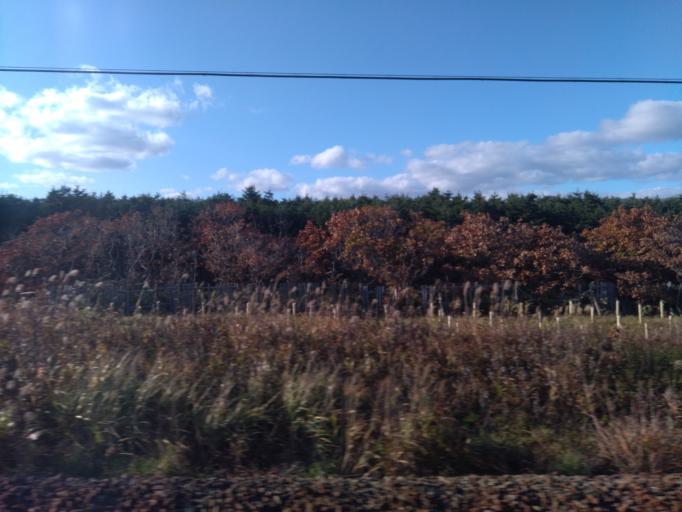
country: JP
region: Hokkaido
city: Niseko Town
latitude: 42.5478
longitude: 140.4145
